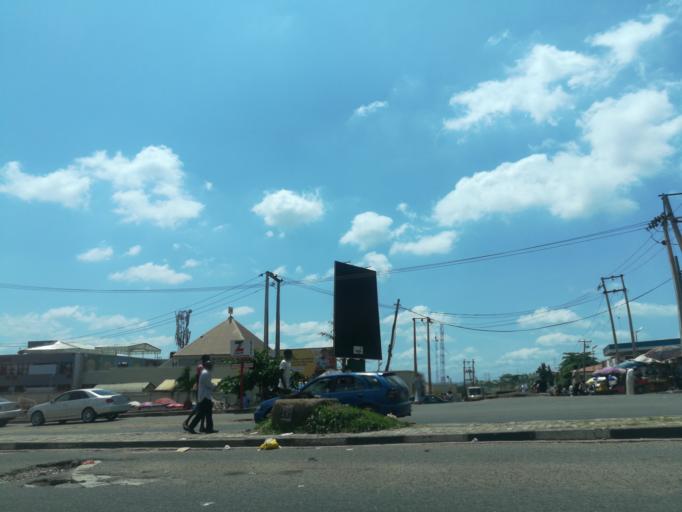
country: NG
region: Oyo
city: Ibadan
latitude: 7.3668
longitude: 3.8613
